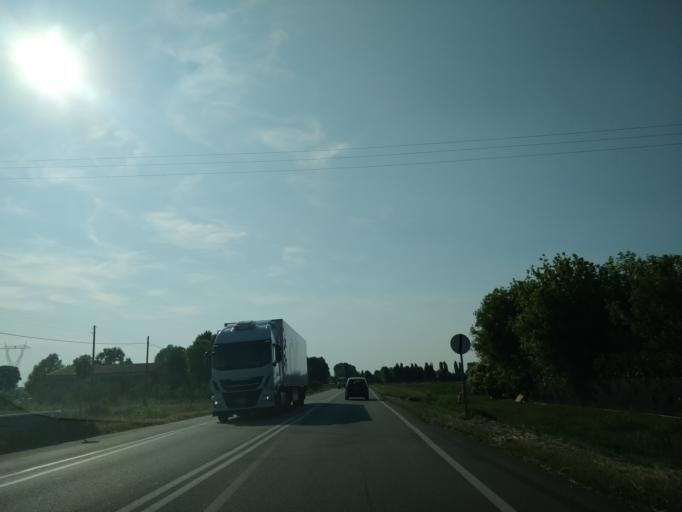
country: IT
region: Emilia-Romagna
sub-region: Provincia di Bologna
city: Castel Maggiore
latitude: 44.6007
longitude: 11.3453
